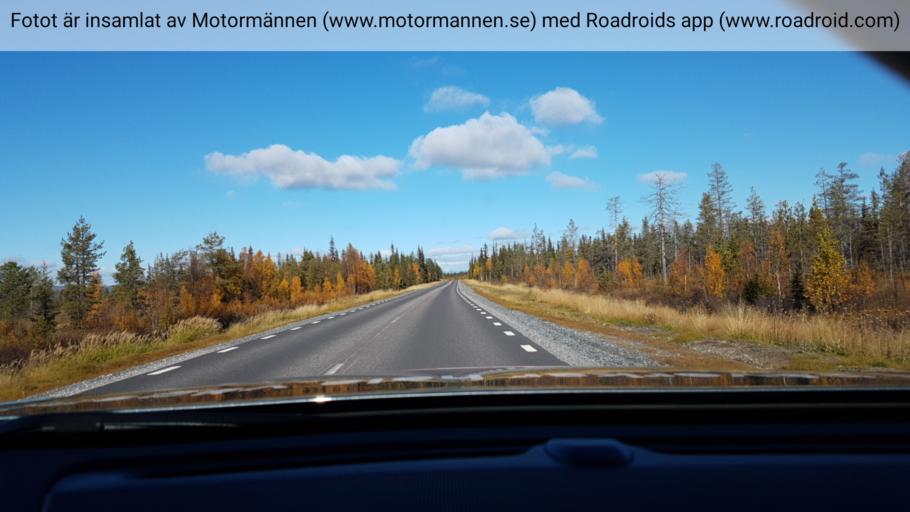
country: SE
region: Norrbotten
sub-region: Gallivare Kommun
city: Gaellivare
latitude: 66.9862
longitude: 20.7416
